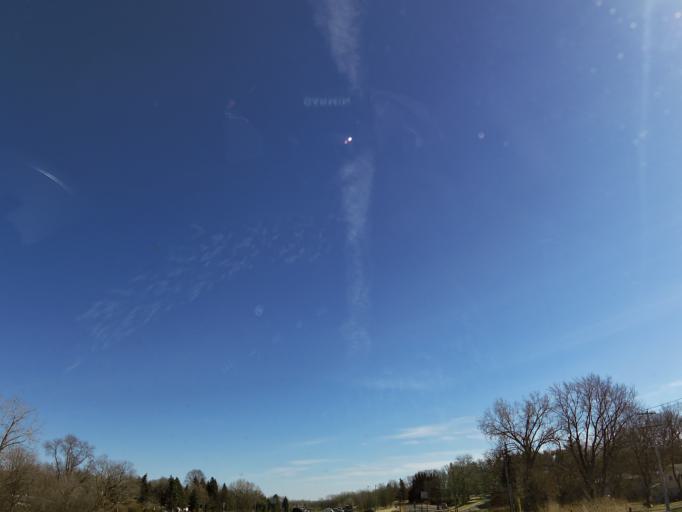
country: US
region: Minnesota
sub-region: Hennepin County
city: Plymouth
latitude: 44.9957
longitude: -93.4381
